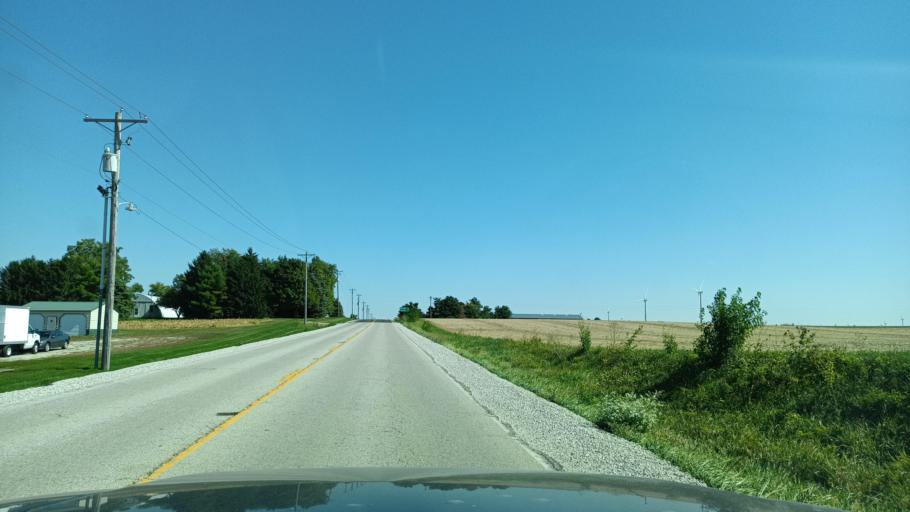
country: US
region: Illinois
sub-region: McLean County
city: Danvers
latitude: 40.5825
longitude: -89.1218
